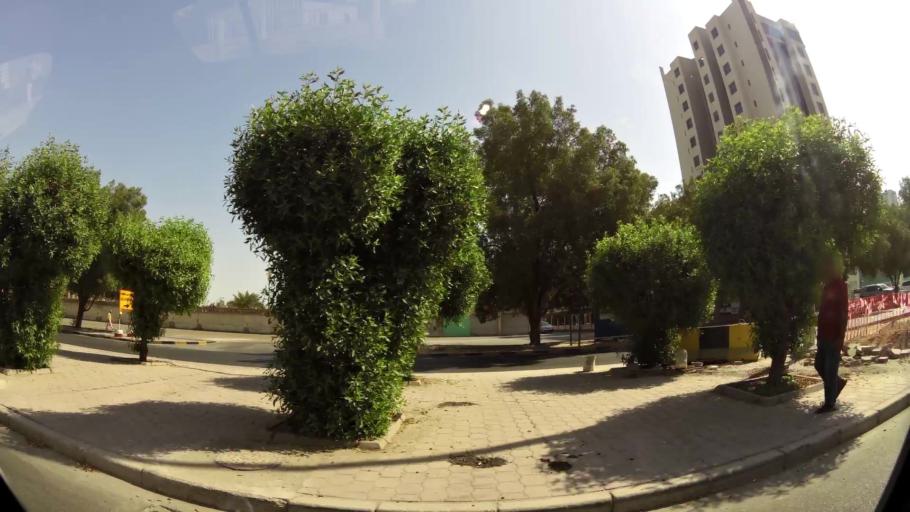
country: KW
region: Al Asimah
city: Ad Dasmah
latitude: 29.3823
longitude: 47.9942
